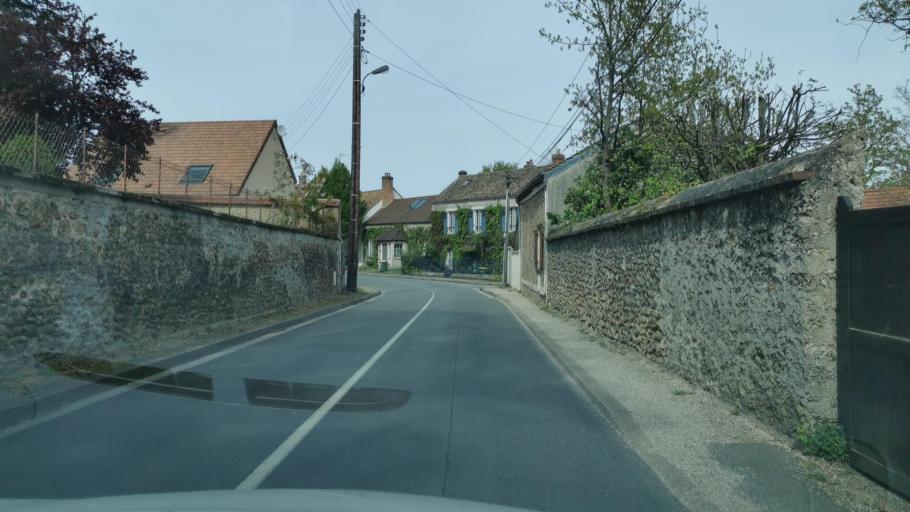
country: FR
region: Ile-de-France
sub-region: Departement des Yvelines
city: Jouars-Pontchartrain
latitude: 48.7760
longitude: 1.8774
